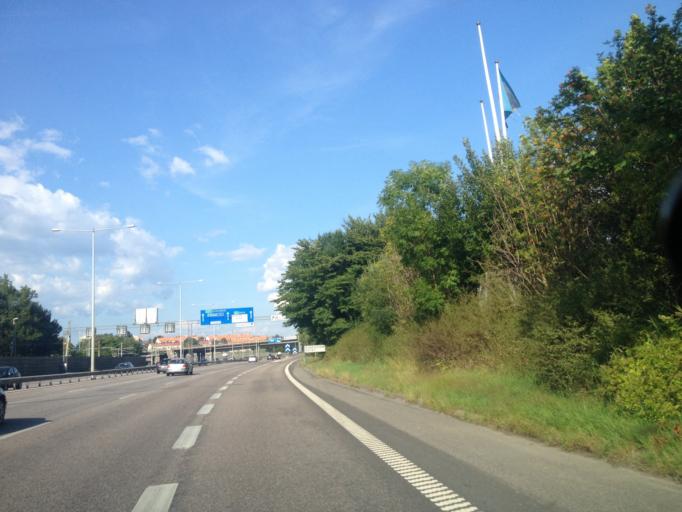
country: SE
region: Vaestra Goetaland
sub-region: Goteborg
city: Majorna
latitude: 57.6790
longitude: 11.8987
